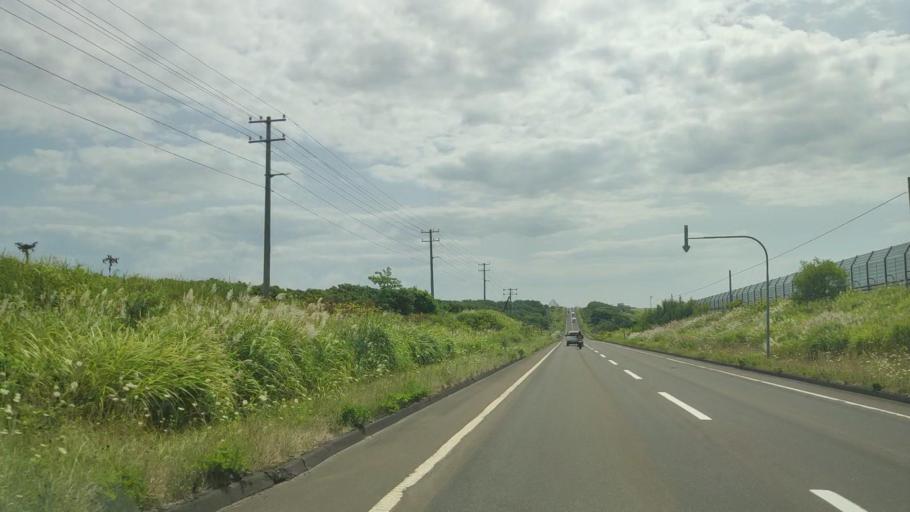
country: JP
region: Hokkaido
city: Rumoi
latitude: 44.4351
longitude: 141.7508
